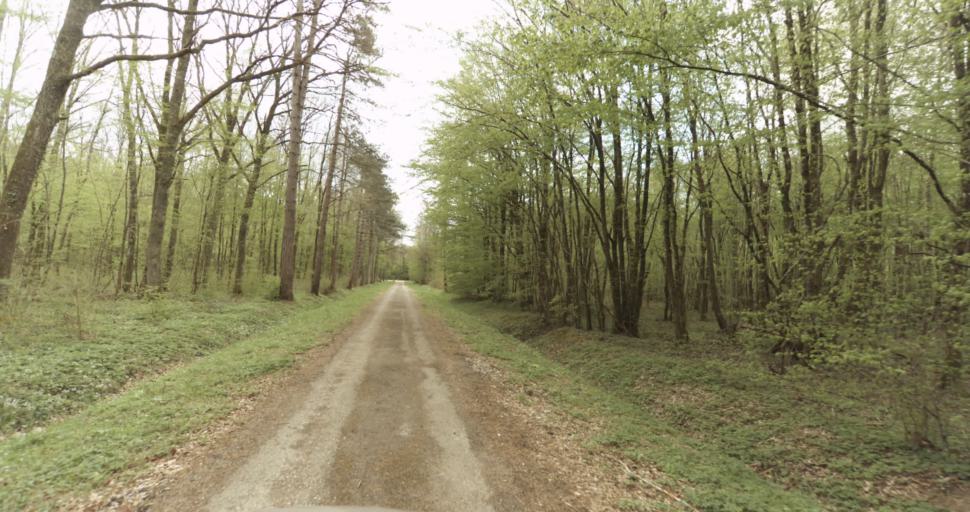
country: FR
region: Bourgogne
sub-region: Departement de la Cote-d'Or
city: Auxonne
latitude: 47.1556
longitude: 5.4224
